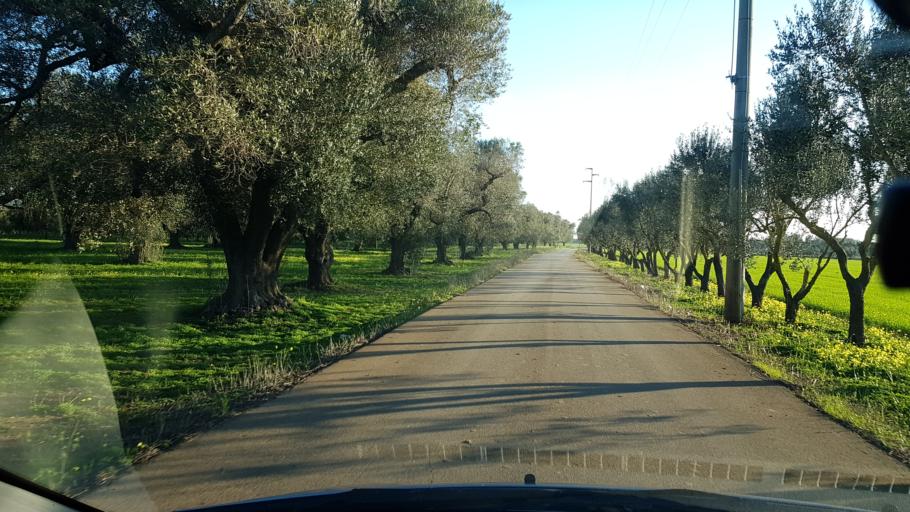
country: IT
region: Apulia
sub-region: Provincia di Brindisi
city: Mesagne
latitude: 40.5579
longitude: 17.8643
